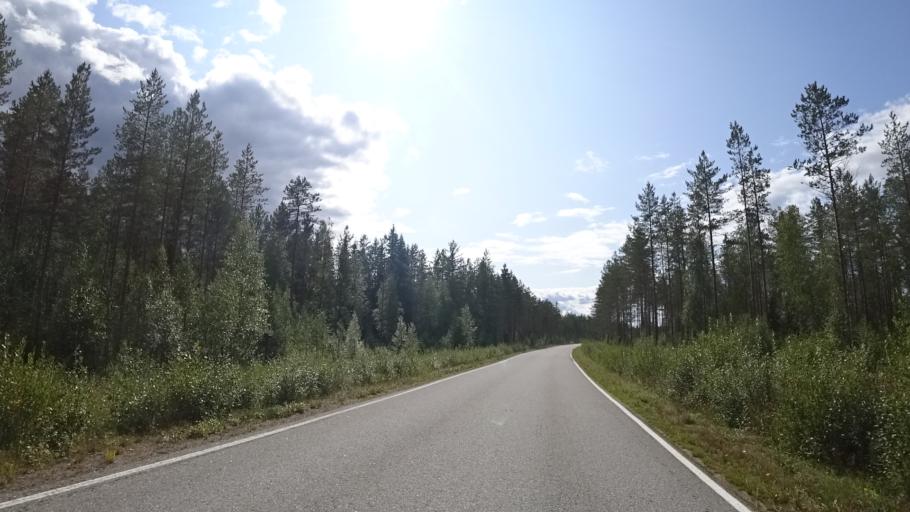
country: FI
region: North Karelia
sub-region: Joensuu
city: Ilomantsi
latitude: 62.4142
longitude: 31.0053
